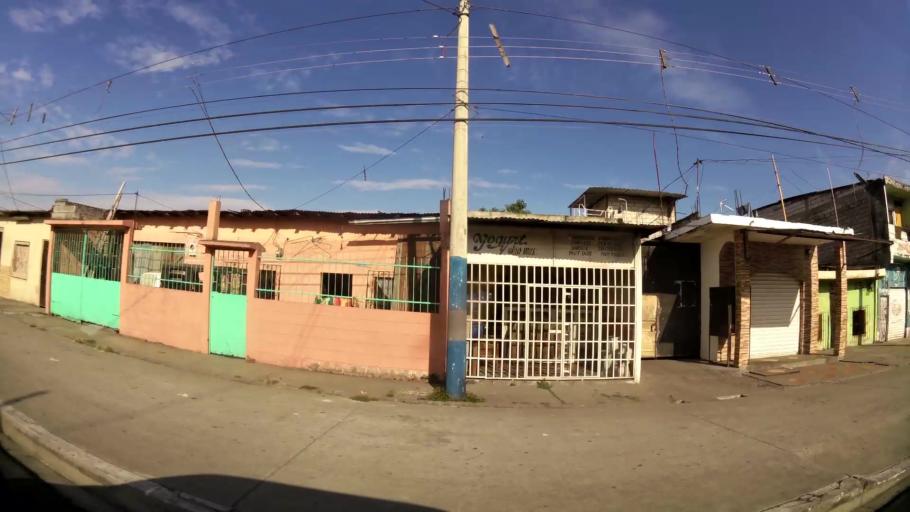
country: EC
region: Guayas
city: Guayaquil
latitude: -2.2195
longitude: -79.9169
